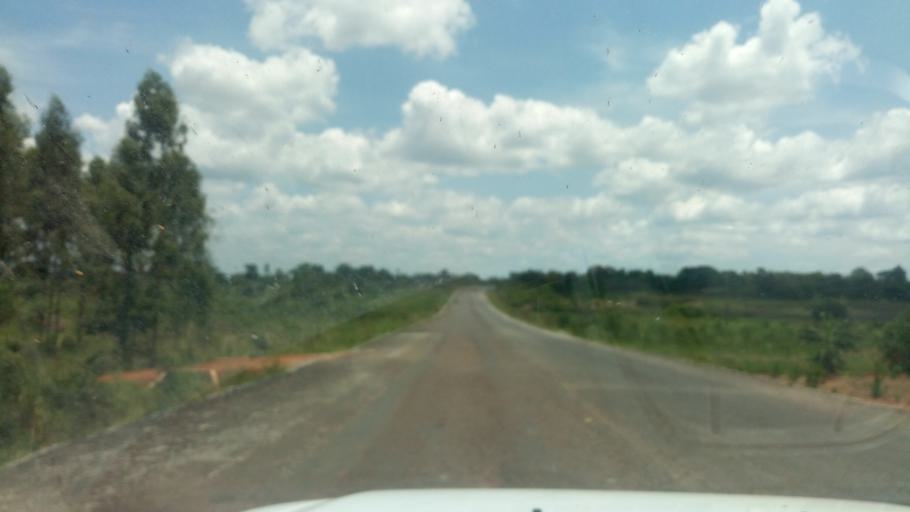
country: UG
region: Western Region
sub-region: Kiryandongo District
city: Kiryandongo
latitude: 1.7902
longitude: 31.9394
